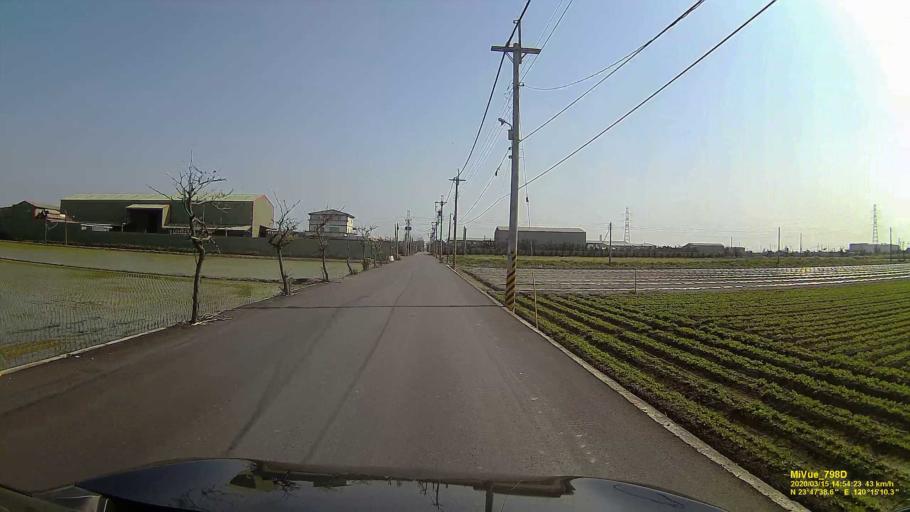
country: TW
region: Taiwan
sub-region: Yunlin
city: Douliu
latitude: 23.7938
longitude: 120.2529
